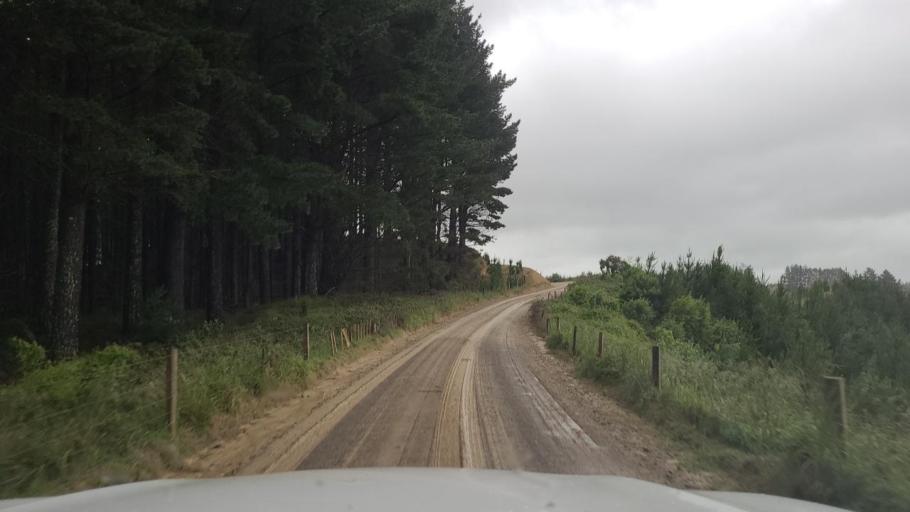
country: NZ
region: Hawke's Bay
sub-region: Napier City
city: Napier
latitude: -39.2834
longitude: 176.8994
